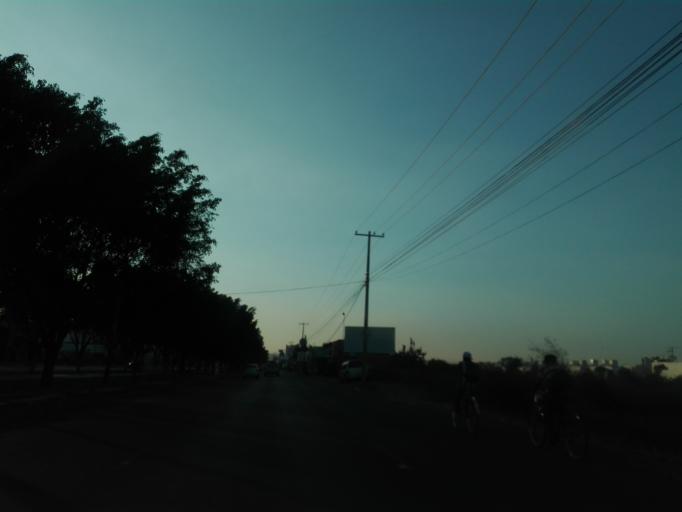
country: MX
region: Guanajuato
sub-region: Leon
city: Medina
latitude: 21.1274
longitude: -101.6411
